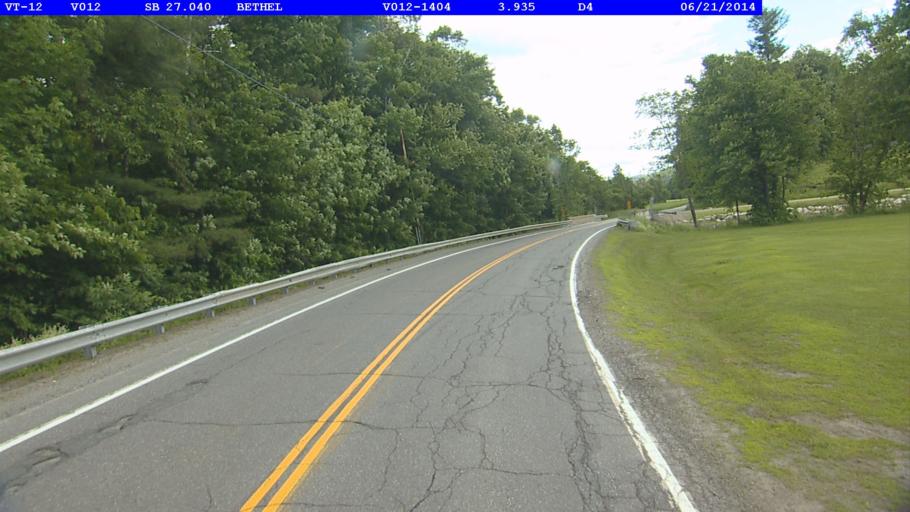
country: US
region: Vermont
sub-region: Orange County
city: Randolph
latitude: 43.8543
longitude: -72.6471
